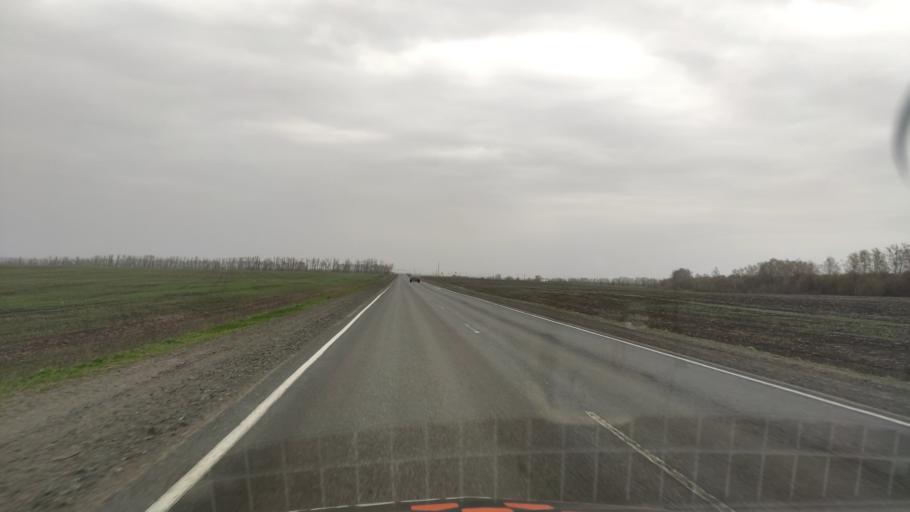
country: RU
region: Kursk
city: Gorshechnoye
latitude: 51.5449
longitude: 38.0269
